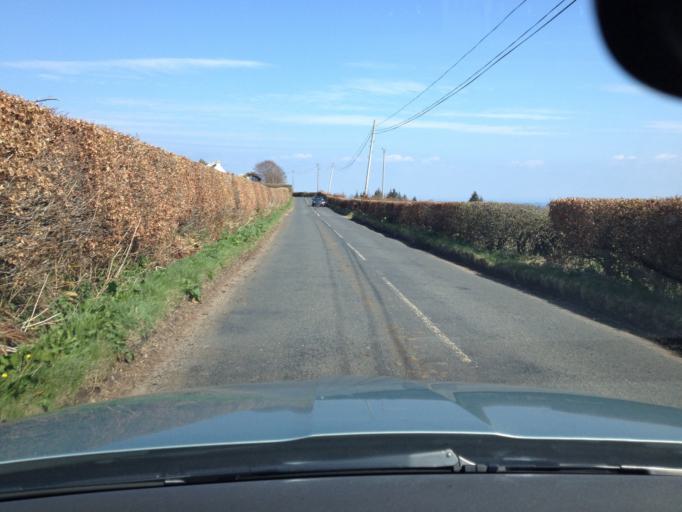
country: GB
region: Scotland
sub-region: North Ayrshire
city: Lamlash
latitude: 55.4553
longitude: -5.0934
